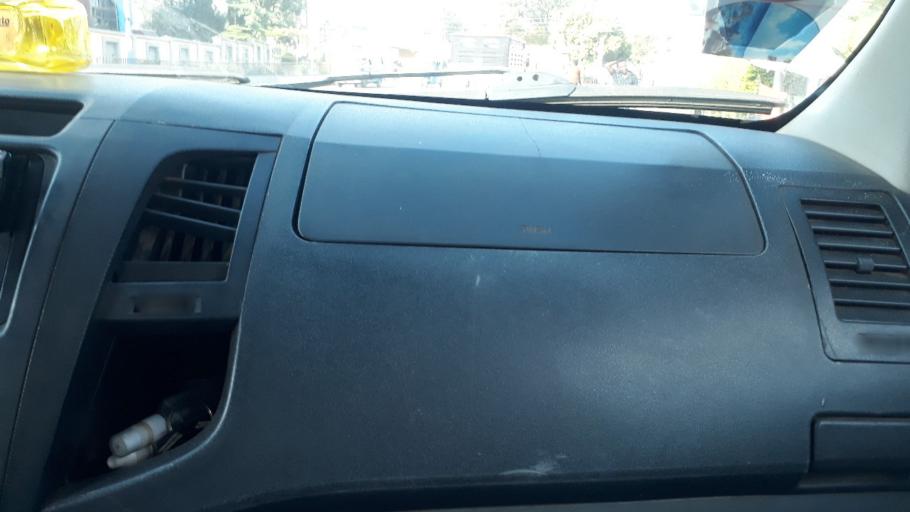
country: ET
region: Oromiya
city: Jima
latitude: 7.6742
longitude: 36.8528
